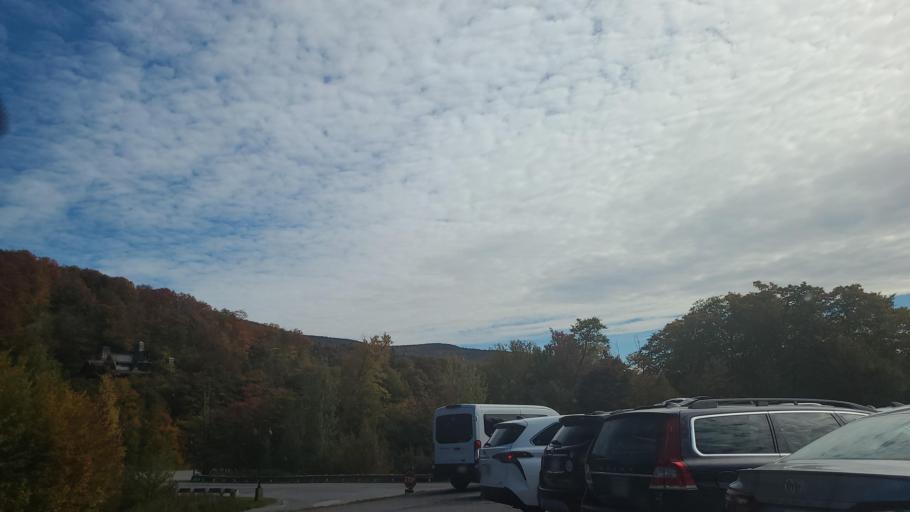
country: US
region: Vermont
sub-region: Lamoille County
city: Johnson
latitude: 44.5320
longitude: -72.7879
